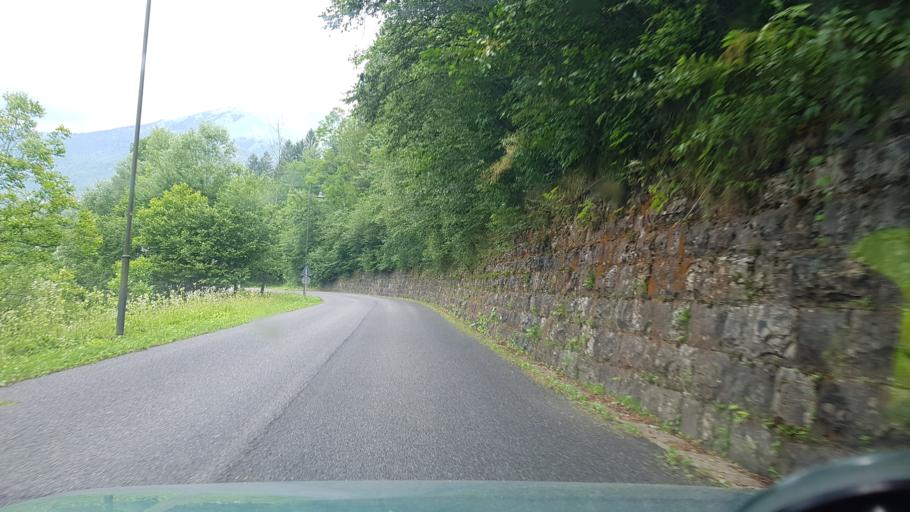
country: IT
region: Friuli Venezia Giulia
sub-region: Provincia di Udine
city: Lusevera
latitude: 46.2617
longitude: 13.2581
